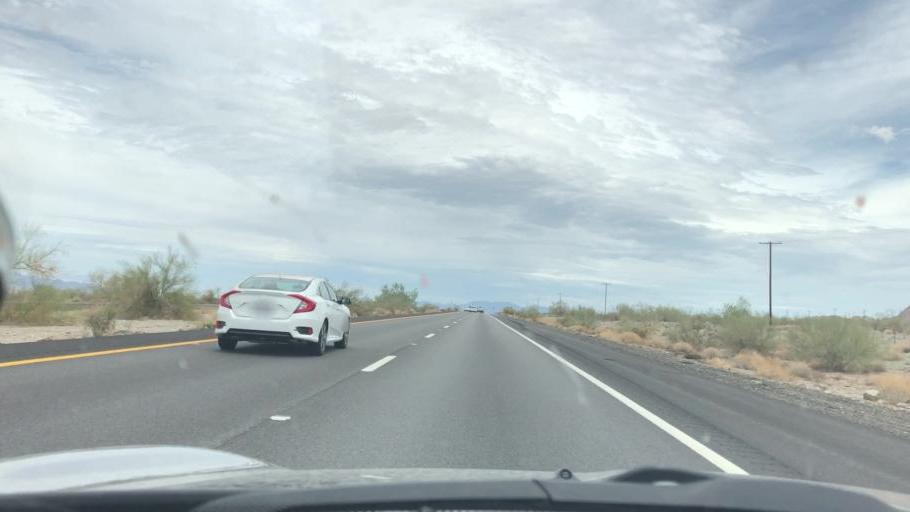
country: US
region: California
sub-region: Imperial County
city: Niland
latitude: 33.6936
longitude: -115.4914
